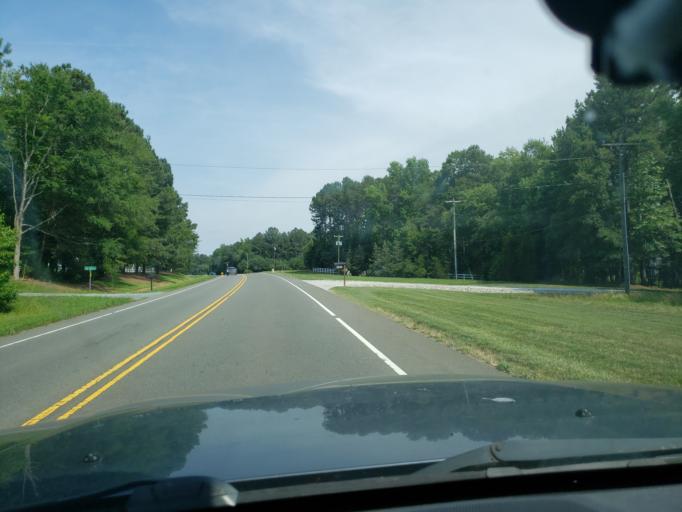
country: US
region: North Carolina
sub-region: Orange County
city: Carrboro
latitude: 35.9232
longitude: -79.1926
